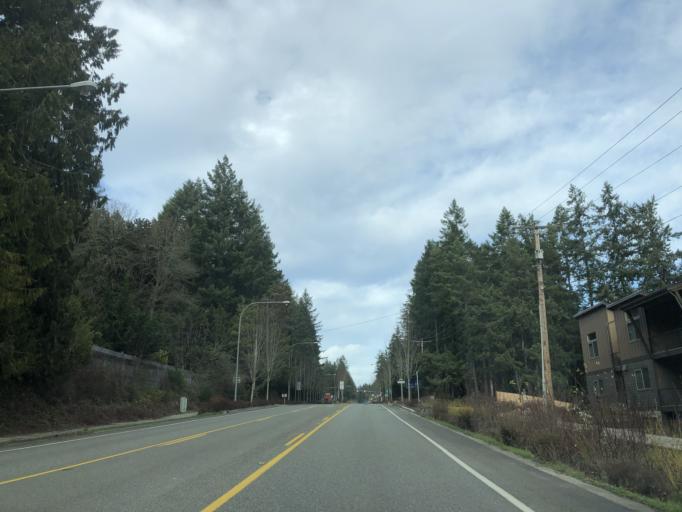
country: US
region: Washington
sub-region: Kitsap County
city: Poulsbo
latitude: 47.7548
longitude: -122.6530
